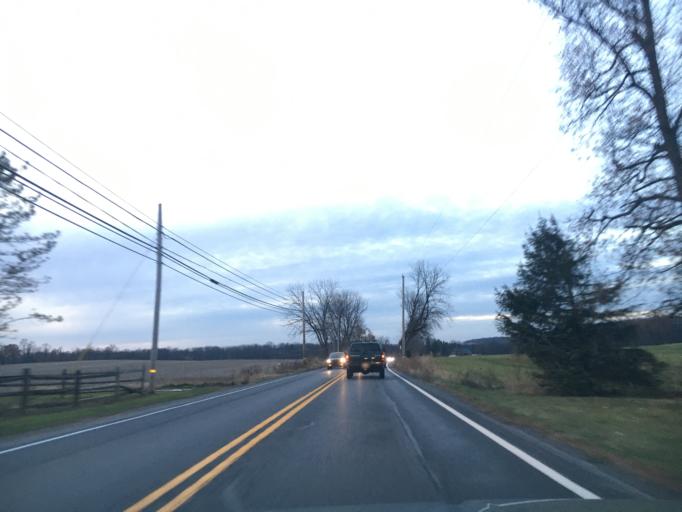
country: US
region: Pennsylvania
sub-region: Lehigh County
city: Egypt
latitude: 40.6545
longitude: -75.5490
